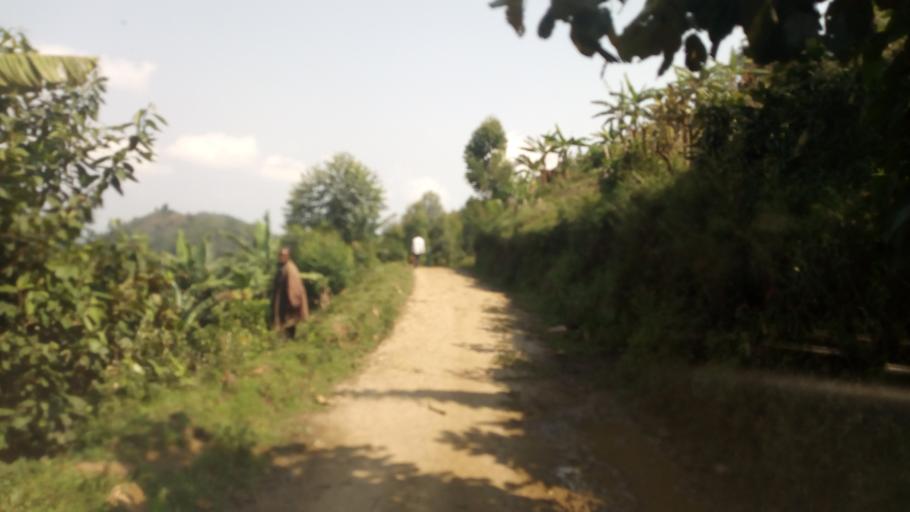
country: UG
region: Western Region
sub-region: Kisoro District
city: Kisoro
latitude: -1.1036
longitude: 29.5902
